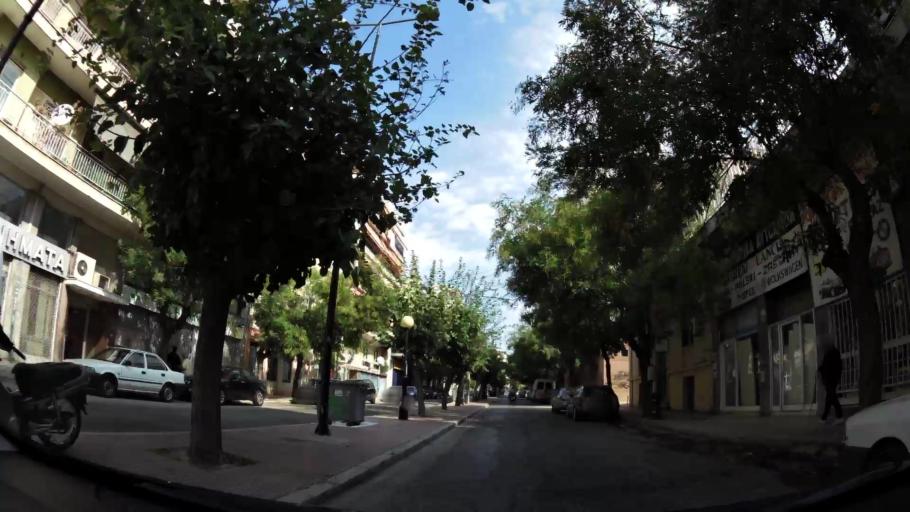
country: GR
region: Attica
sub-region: Nomarchia Athinas
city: Athens
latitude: 37.9882
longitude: 23.7153
